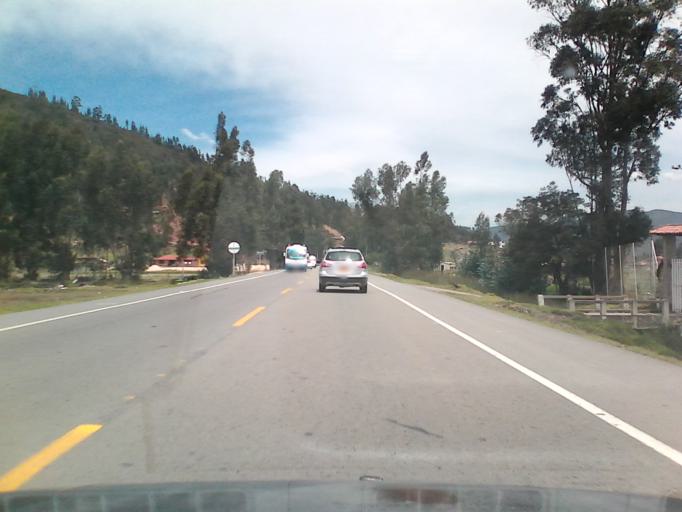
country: CO
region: Boyaca
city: Tibasosa
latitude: 5.7833
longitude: -72.9967
